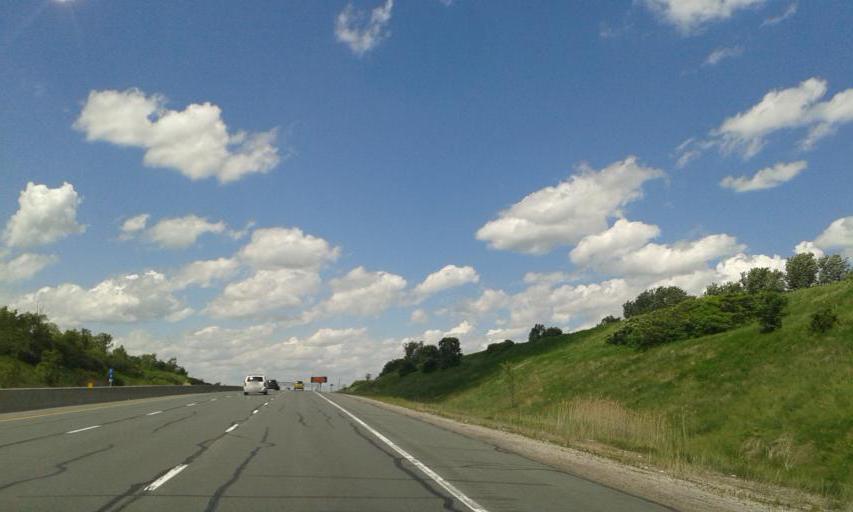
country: CA
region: Ontario
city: Burlington
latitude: 43.3654
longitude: -79.8320
